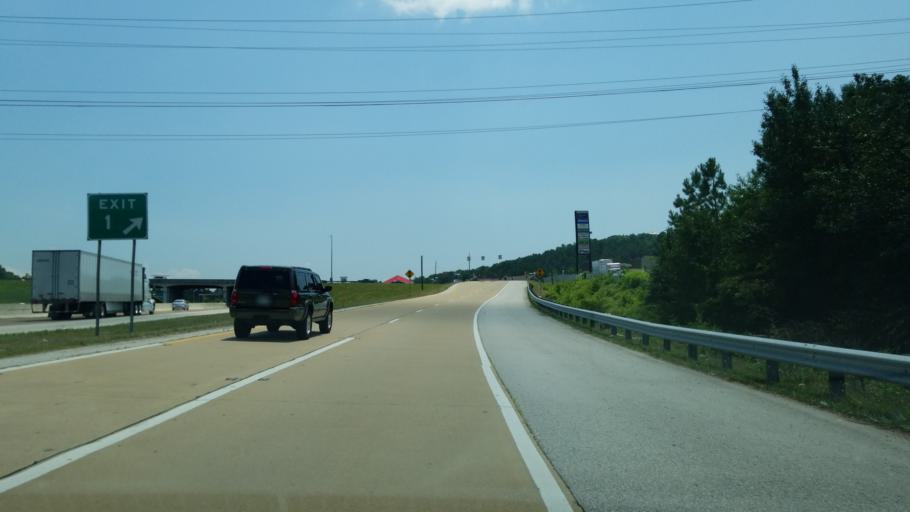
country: US
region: Tennessee
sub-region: Hamilton County
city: East Brainerd
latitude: 35.0342
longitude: -85.1835
